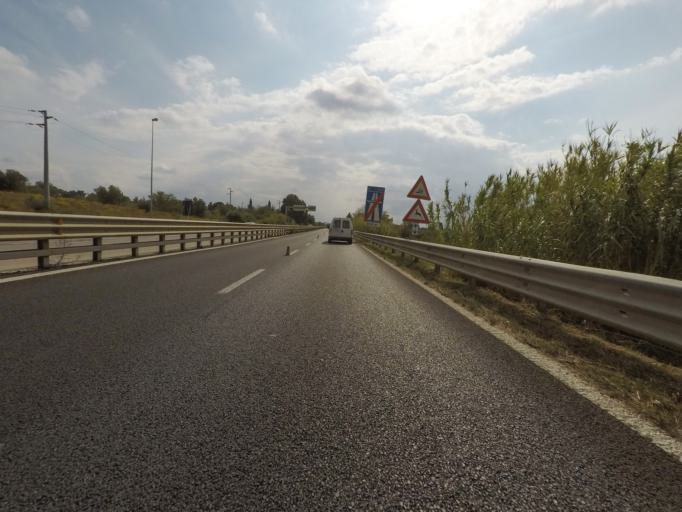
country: IT
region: Tuscany
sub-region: Provincia di Grosseto
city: Grosseto
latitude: 42.7275
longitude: 11.1364
